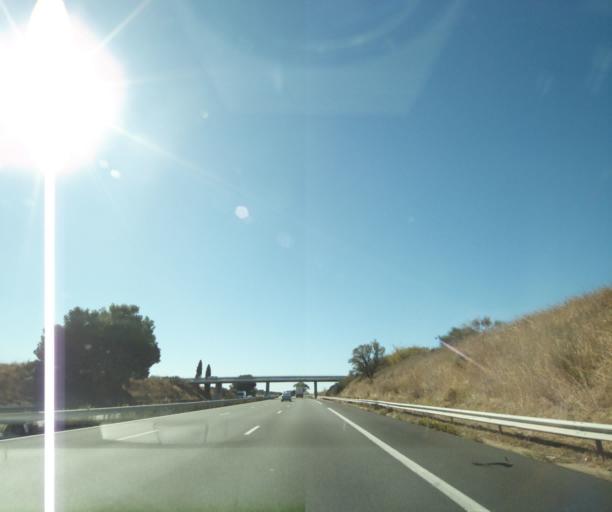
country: FR
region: Languedoc-Roussillon
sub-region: Departement de l'Herault
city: Pomerols
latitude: 43.4072
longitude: 3.4911
